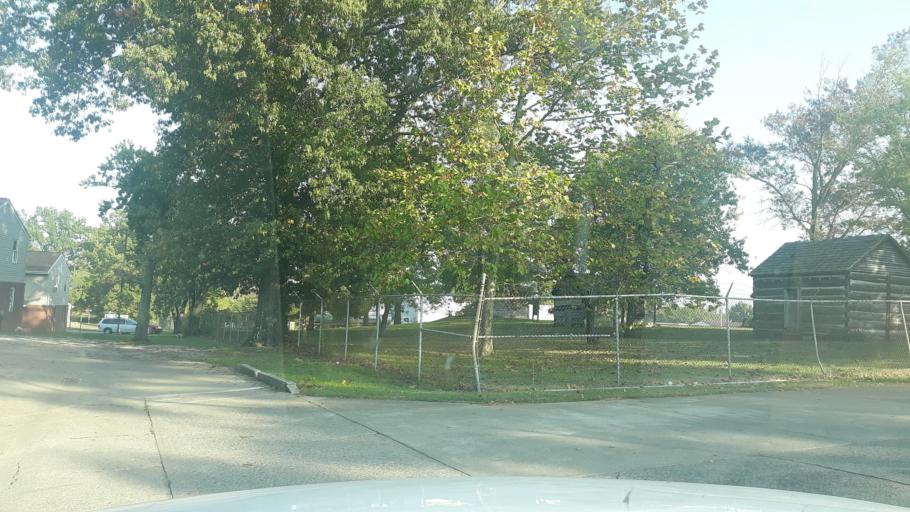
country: US
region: Illinois
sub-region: Saline County
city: Harrisburg
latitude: 37.7194
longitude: -88.5525
